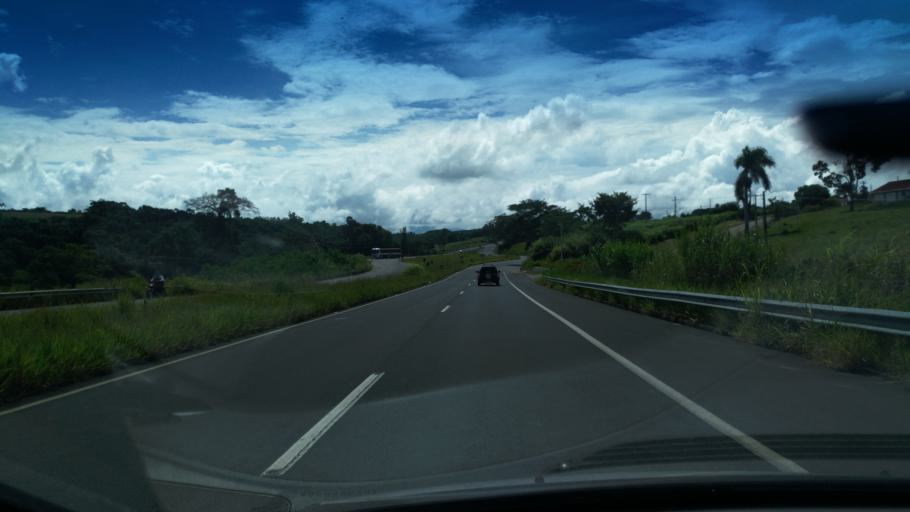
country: BR
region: Sao Paulo
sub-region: Santo Antonio Do Jardim
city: Espirito Santo do Pinhal
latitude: -22.1667
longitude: -46.7387
